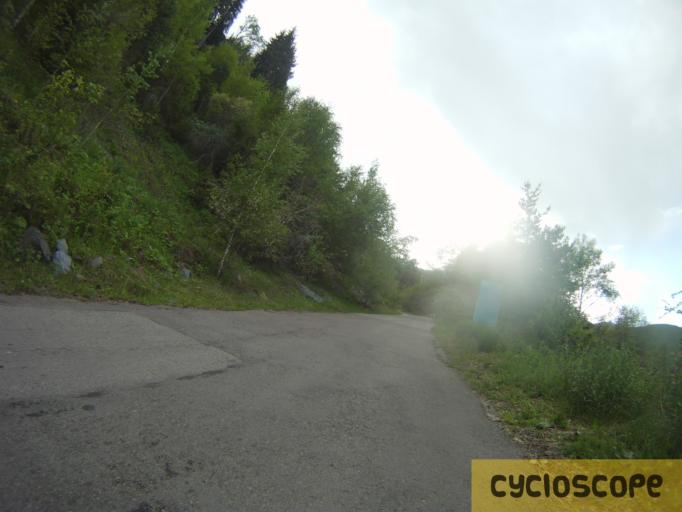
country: KZ
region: Almaty Oblysy
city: Esik
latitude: 43.2713
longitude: 77.5017
